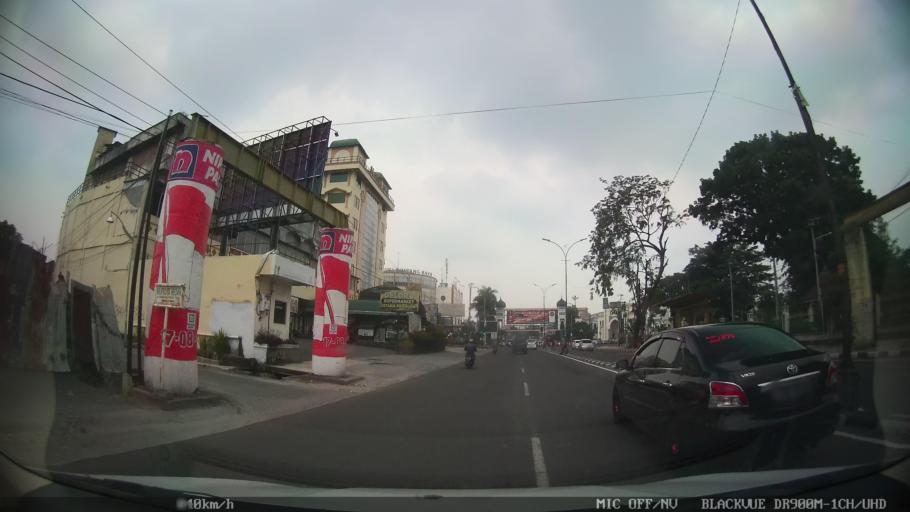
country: ID
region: North Sumatra
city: Medan
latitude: 3.5773
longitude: 98.6870
